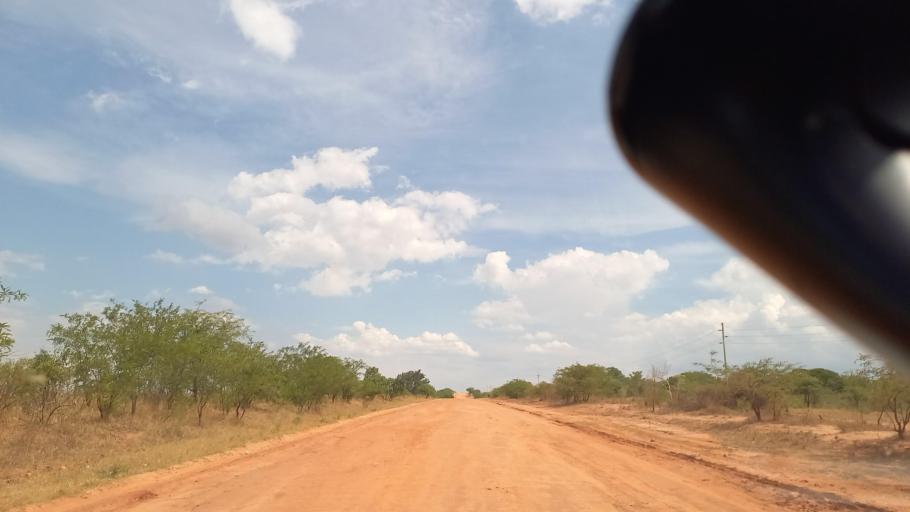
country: ZM
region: Lusaka
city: Kafue
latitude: -16.1241
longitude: 28.0426
